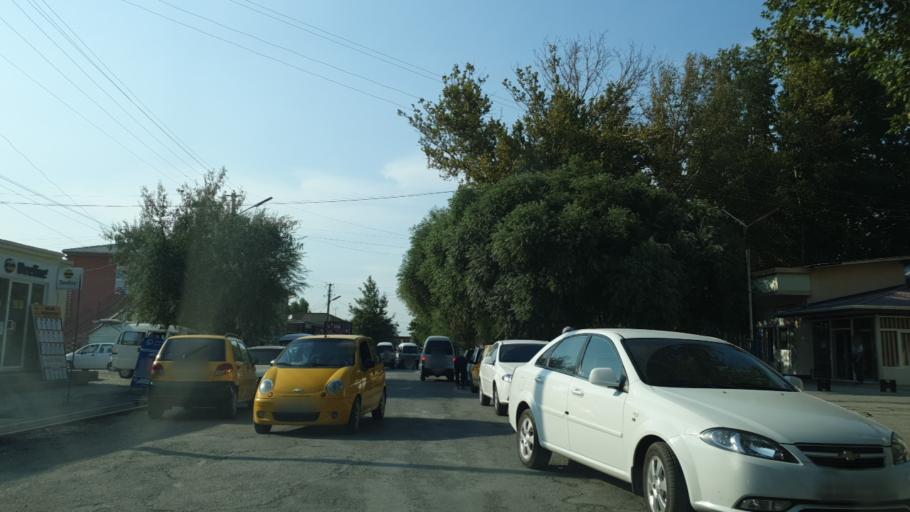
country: UZ
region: Fergana
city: Yaypan
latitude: 40.3784
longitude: 70.8111
